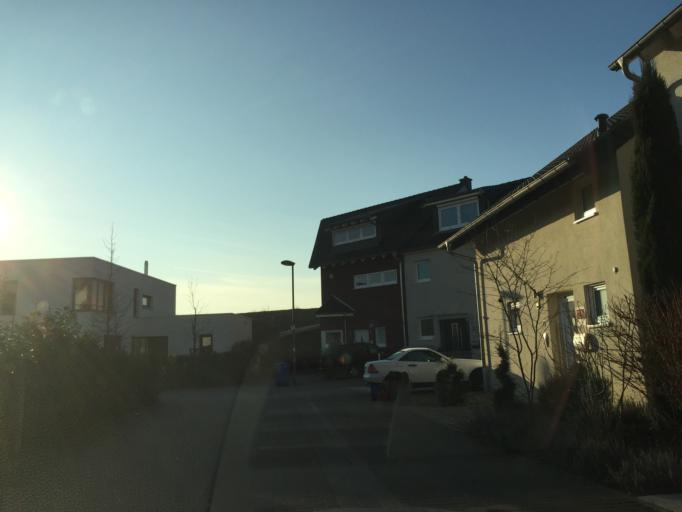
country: DE
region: Baden-Wuerttemberg
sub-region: Karlsruhe Region
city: Oftersheim
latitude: 49.3719
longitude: 8.5713
